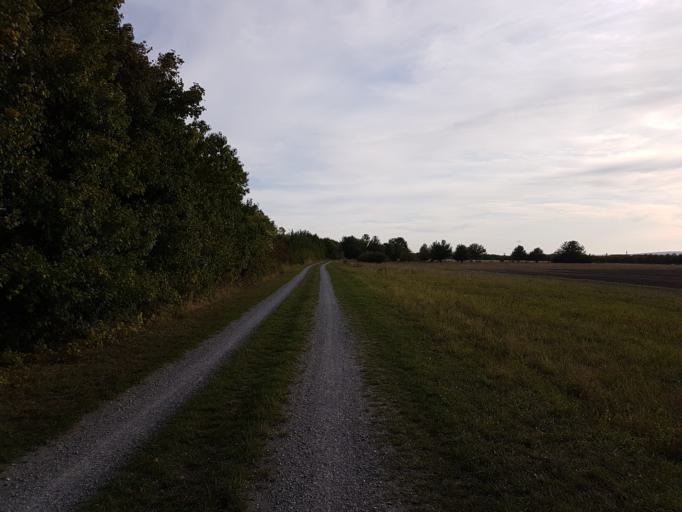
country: DE
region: Lower Saxony
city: Laatzen
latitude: 52.3447
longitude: 9.8498
